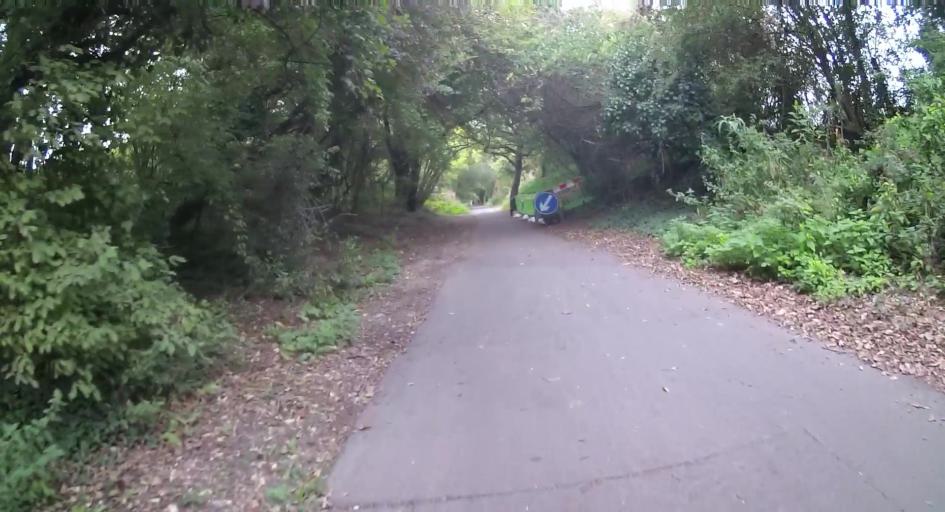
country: GB
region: England
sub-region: Isle of Wight
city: East Cowes
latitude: 50.7483
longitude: -1.2944
